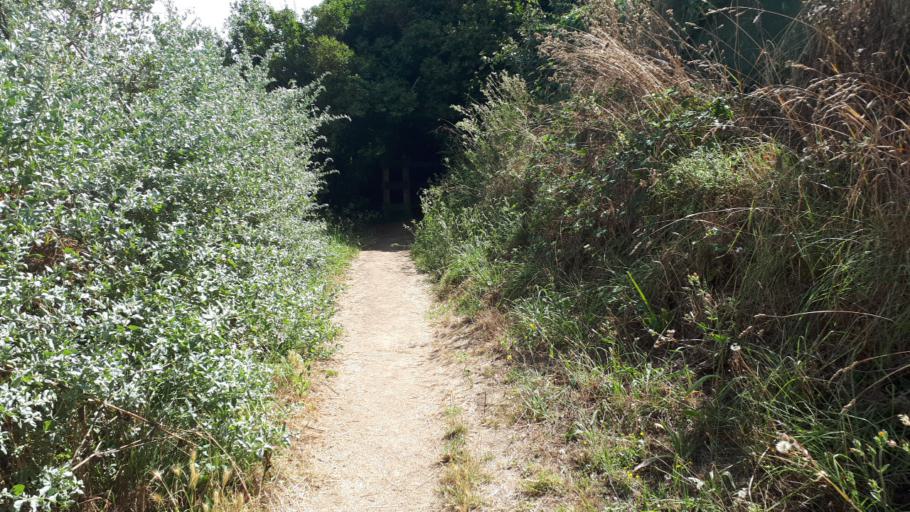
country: FR
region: Brittany
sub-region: Departement des Cotes-d'Armor
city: Etables-sur-Mer
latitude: 48.6342
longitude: -2.8232
